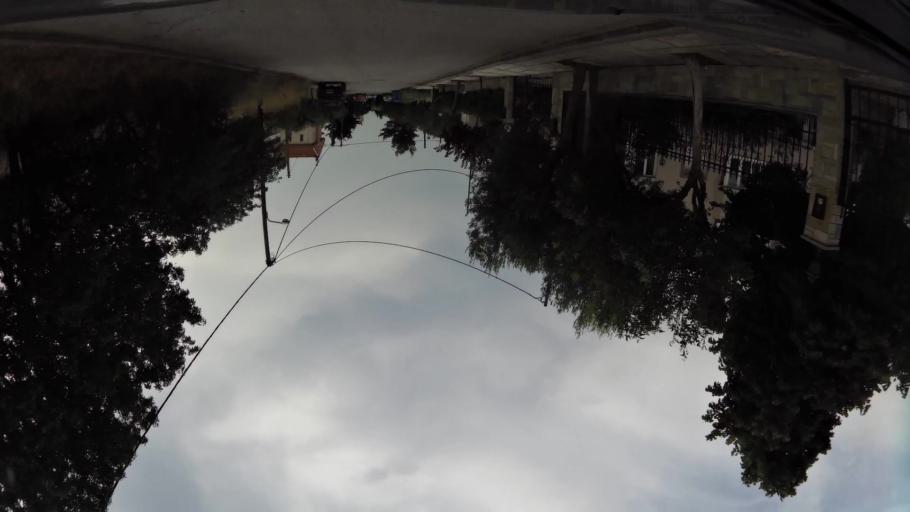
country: GR
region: Central Macedonia
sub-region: Nomos Thessalonikis
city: Oraiokastro
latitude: 40.7130
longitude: 22.9320
